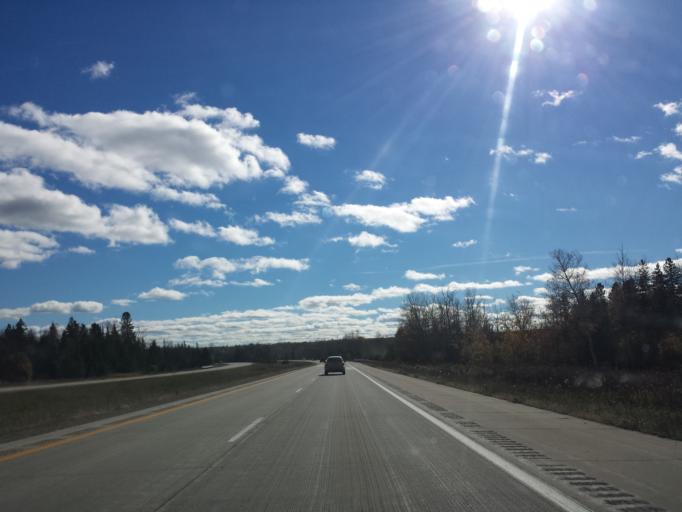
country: US
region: Michigan
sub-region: Cheboygan County
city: Indian River
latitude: 45.5492
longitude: -84.6207
